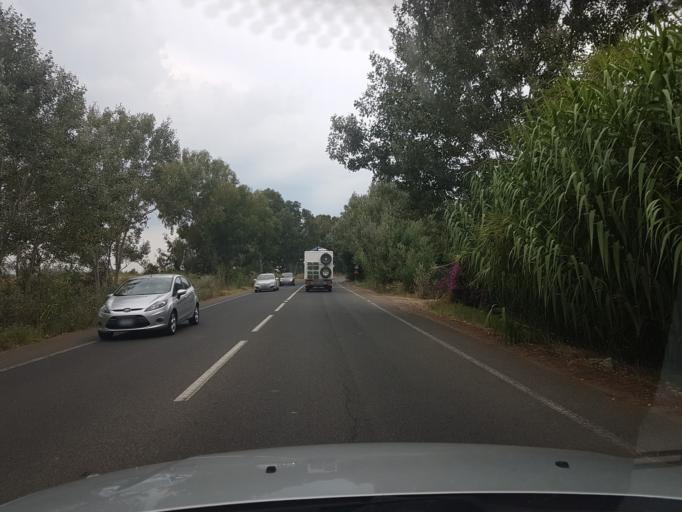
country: IT
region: Sardinia
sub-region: Provincia di Oristano
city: Donigala Fenugheddu
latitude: 39.9240
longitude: 8.5741
